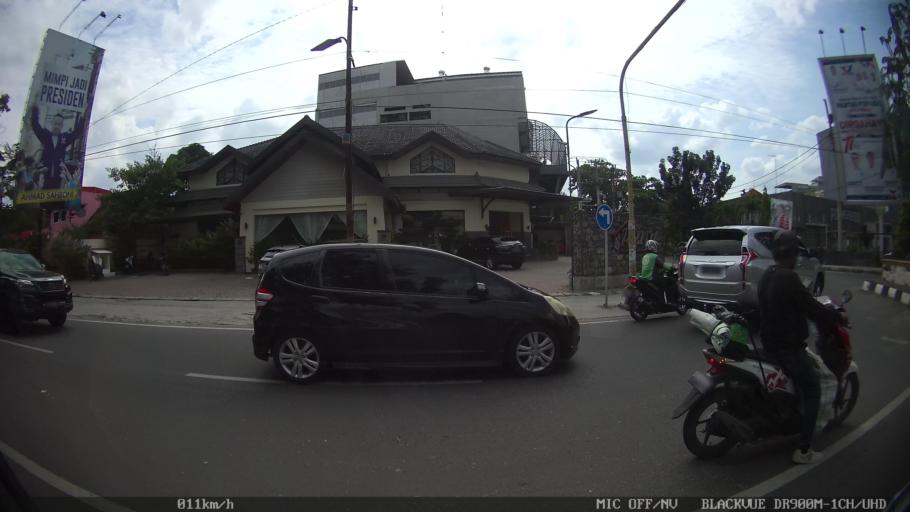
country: ID
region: North Sumatra
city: Medan
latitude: 3.5829
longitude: 98.6671
